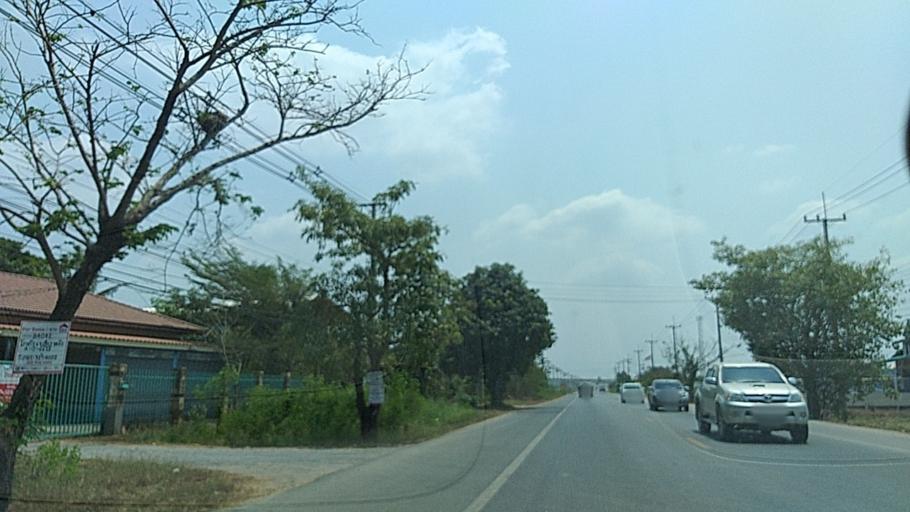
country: TH
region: Chachoengsao
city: Chachoengsao
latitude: 13.7520
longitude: 101.0768
